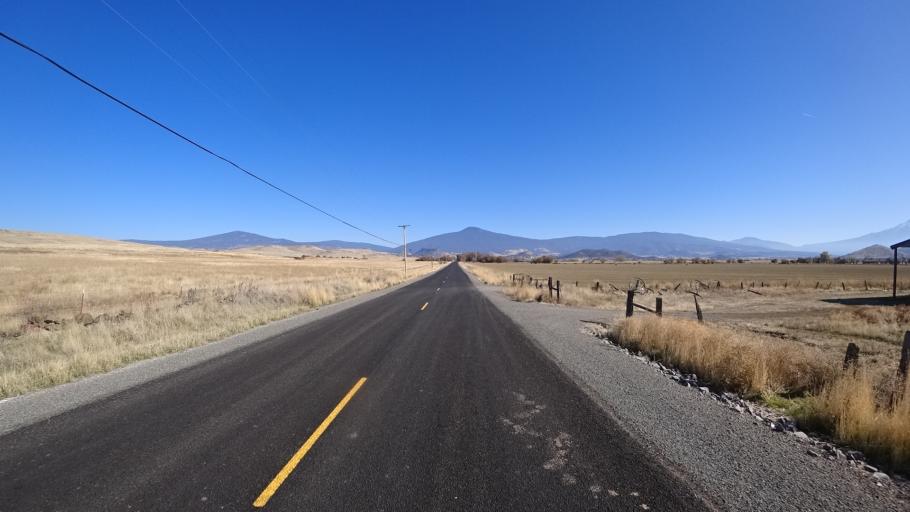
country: US
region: California
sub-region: Siskiyou County
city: Montague
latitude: 41.7263
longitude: -122.4269
